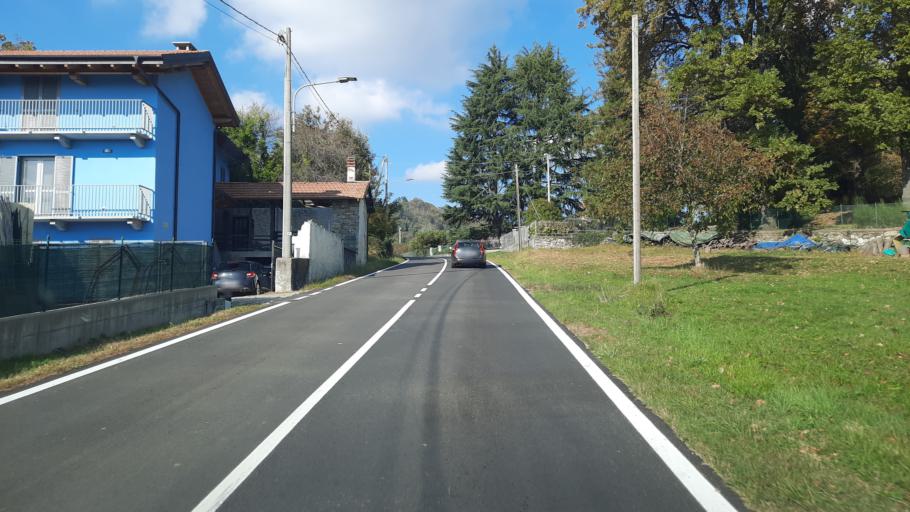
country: IT
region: Piedmont
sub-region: Provincia di Novara
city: Bolzano Novarese
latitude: 45.7662
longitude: 8.4443
